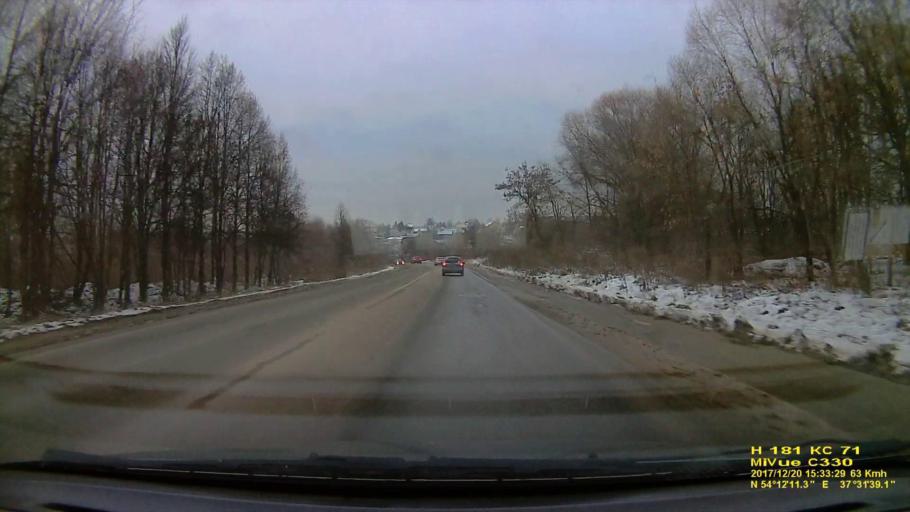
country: RU
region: Tula
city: Barsuki
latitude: 54.2032
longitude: 37.5280
